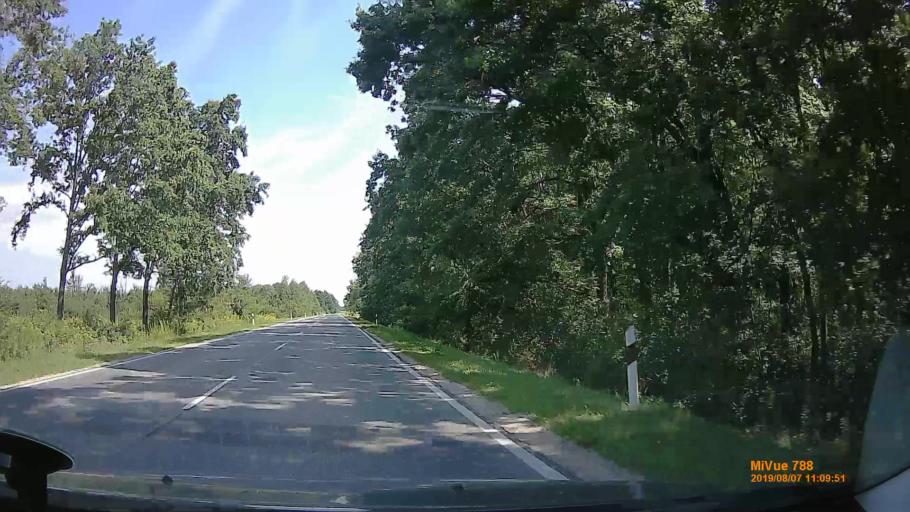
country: HU
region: Zala
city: Lenti
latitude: 46.6568
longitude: 16.4993
